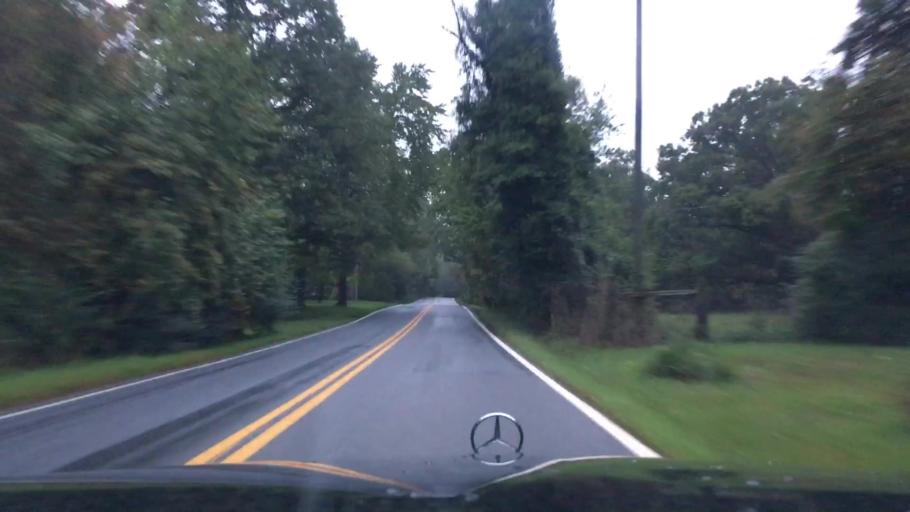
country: US
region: Virginia
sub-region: Campbell County
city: Timberlake
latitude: 37.2431
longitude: -79.2812
